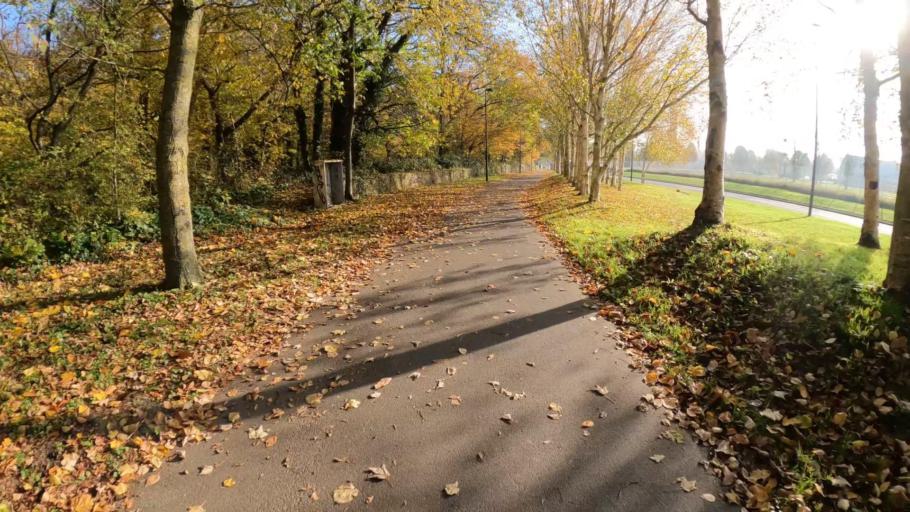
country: FR
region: Lower Normandy
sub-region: Departement du Calvados
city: Herouville-Saint-Clair
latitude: 49.2113
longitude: -0.3387
